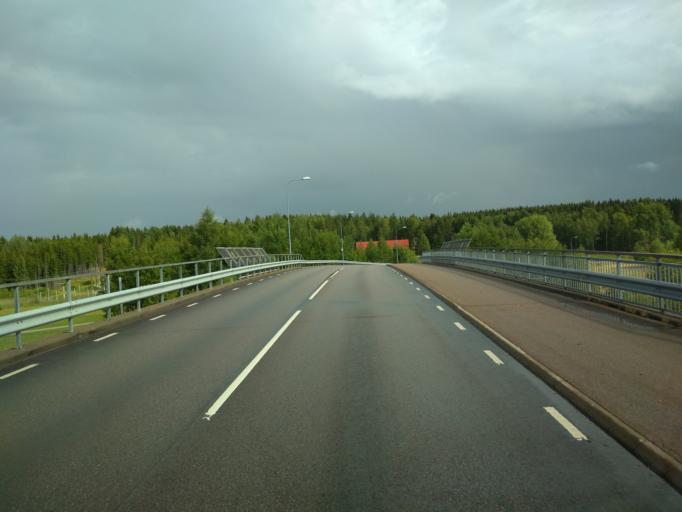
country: SE
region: Vaestmanland
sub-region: Surahammars Kommun
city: Ramnas
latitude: 59.8772
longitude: 16.0820
